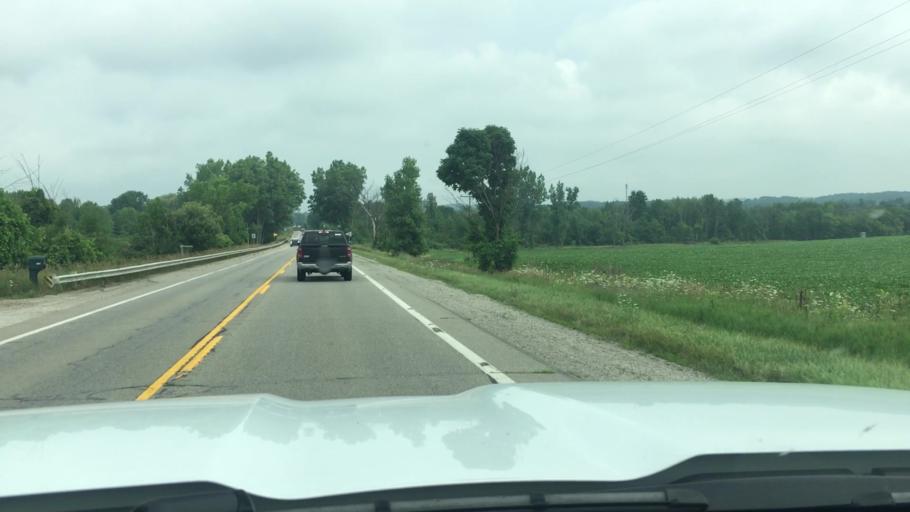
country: US
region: Michigan
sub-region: Sanilac County
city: Brown City
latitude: 43.1426
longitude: -83.0740
